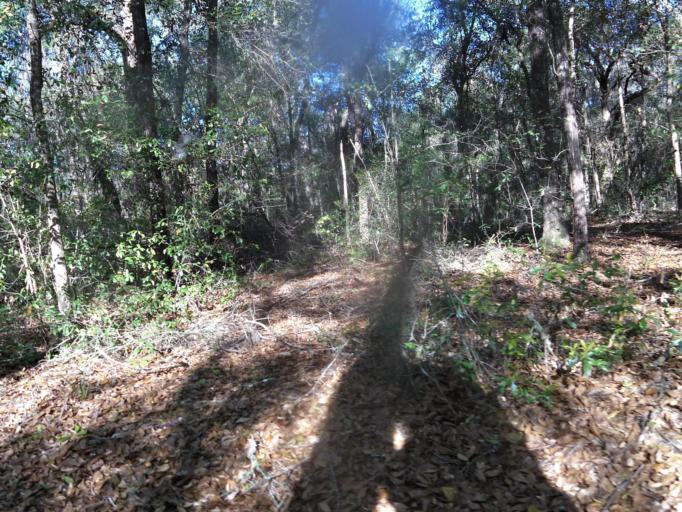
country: US
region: Florida
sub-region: Clay County
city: Keystone Heights
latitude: 29.8189
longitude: -82.0210
